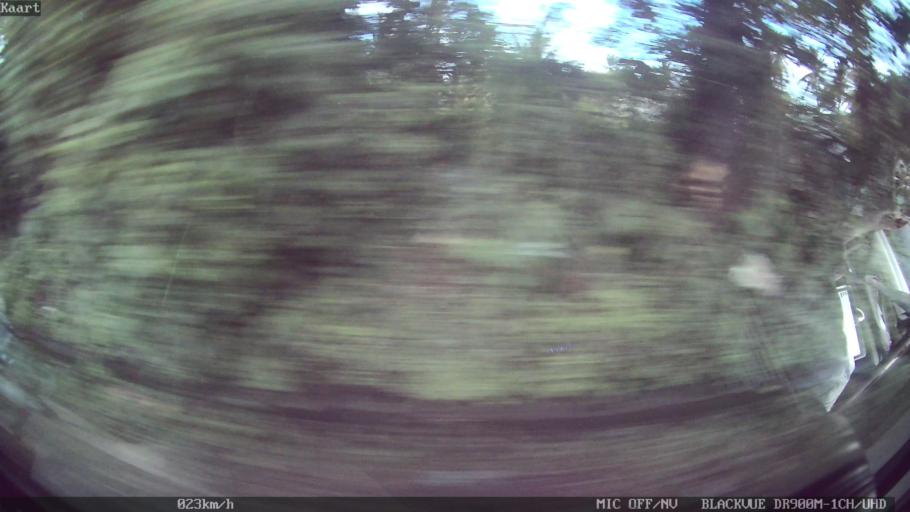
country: ID
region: Bali
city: Banjar Parekan
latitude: -8.5731
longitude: 115.2036
